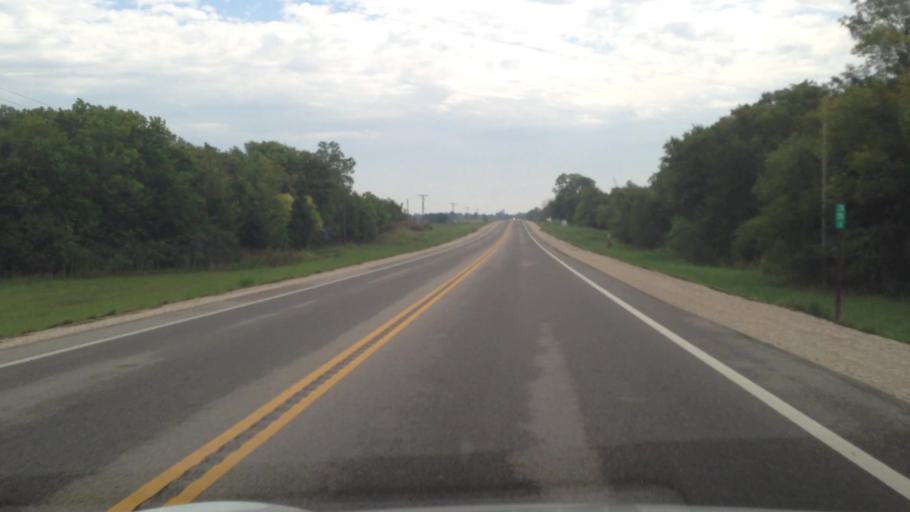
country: US
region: Kansas
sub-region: Allen County
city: Iola
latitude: 37.9065
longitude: -95.0977
